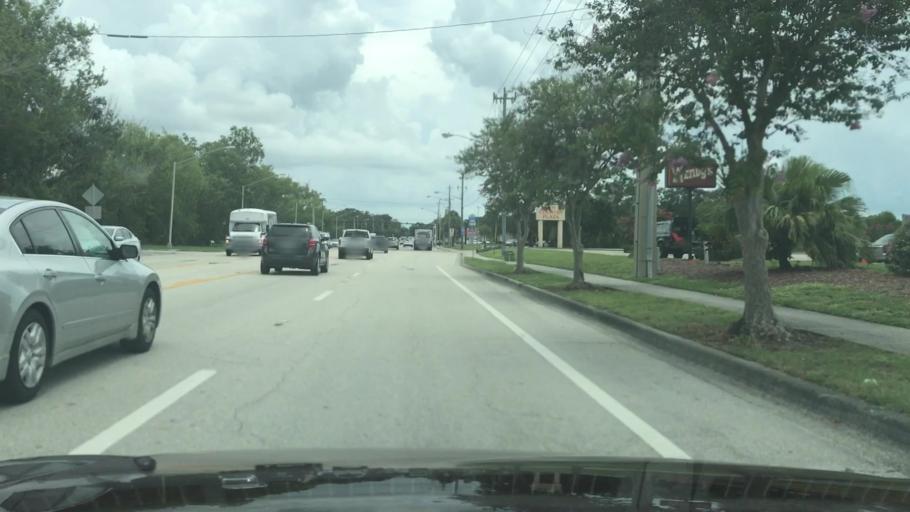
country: US
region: Florida
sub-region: Sarasota County
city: Kensington Park
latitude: 27.3400
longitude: -82.4974
